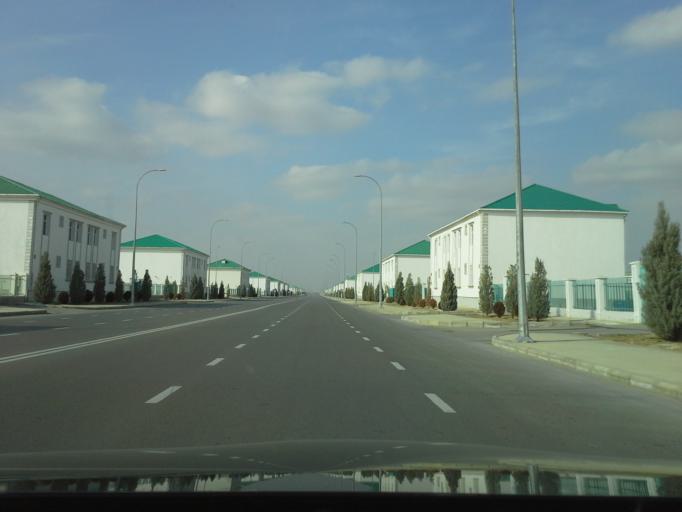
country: TM
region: Ahal
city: Abadan
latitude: 38.0781
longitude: 58.2791
